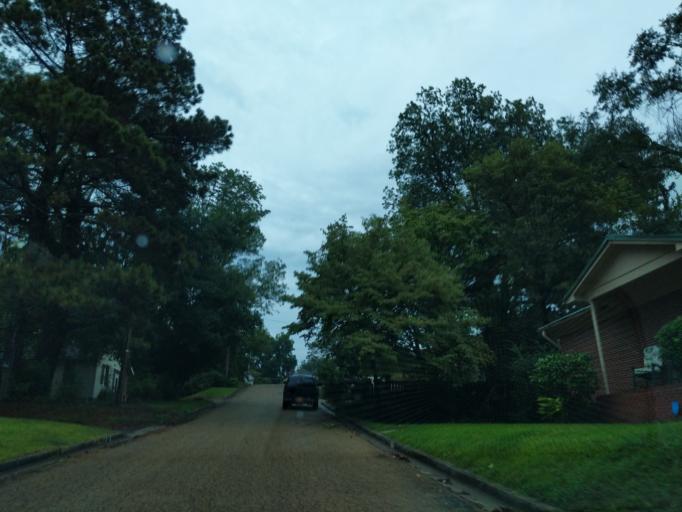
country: US
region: Mississippi
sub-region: Warren County
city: Vicksburg
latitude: 32.3340
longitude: -90.8891
